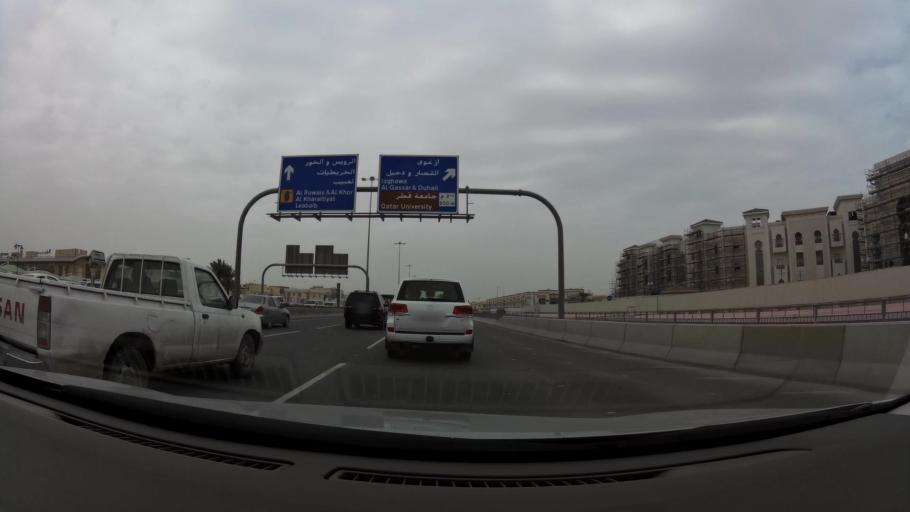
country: QA
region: Baladiyat ar Rayyan
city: Ar Rayyan
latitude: 25.3374
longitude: 51.4617
